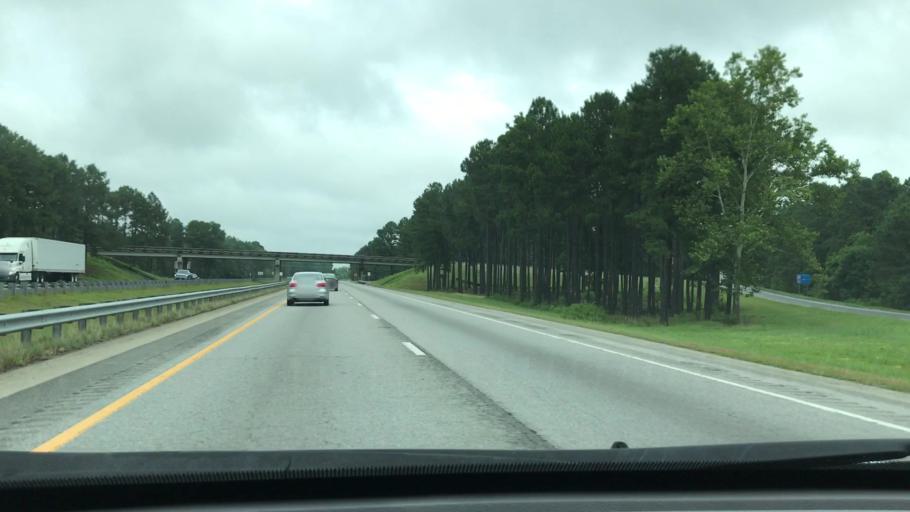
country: US
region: North Carolina
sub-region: Northampton County
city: Gaston
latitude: 36.5231
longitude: -77.5854
